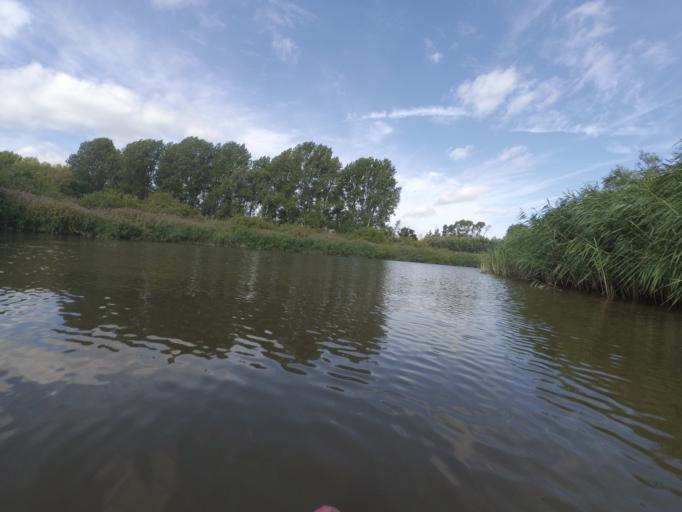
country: NL
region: North Brabant
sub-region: Gemeente Made en Drimmelen
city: Drimmelen
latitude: 51.7386
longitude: 4.7943
